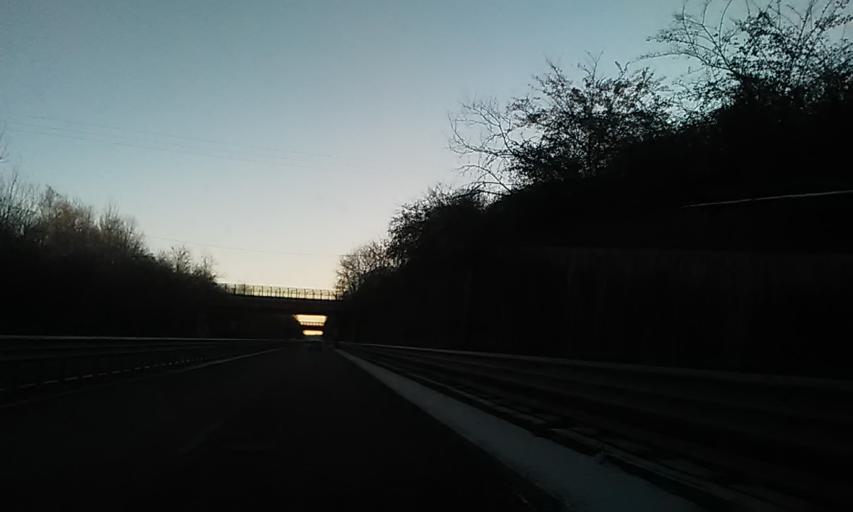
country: IT
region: Piedmont
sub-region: Provincia di Biella
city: Castelletto Cervo
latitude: 45.5522
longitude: 8.2159
